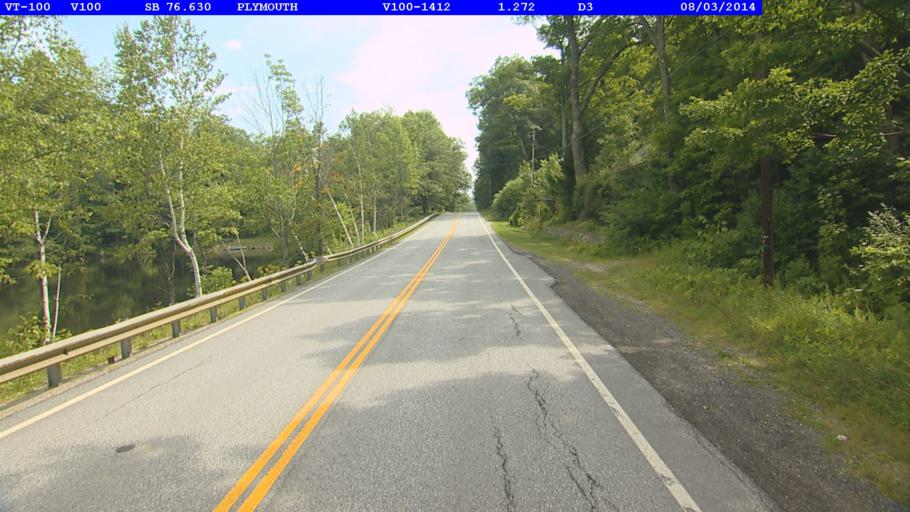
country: US
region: Vermont
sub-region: Windsor County
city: Woodstock
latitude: 43.4809
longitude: -72.7041
